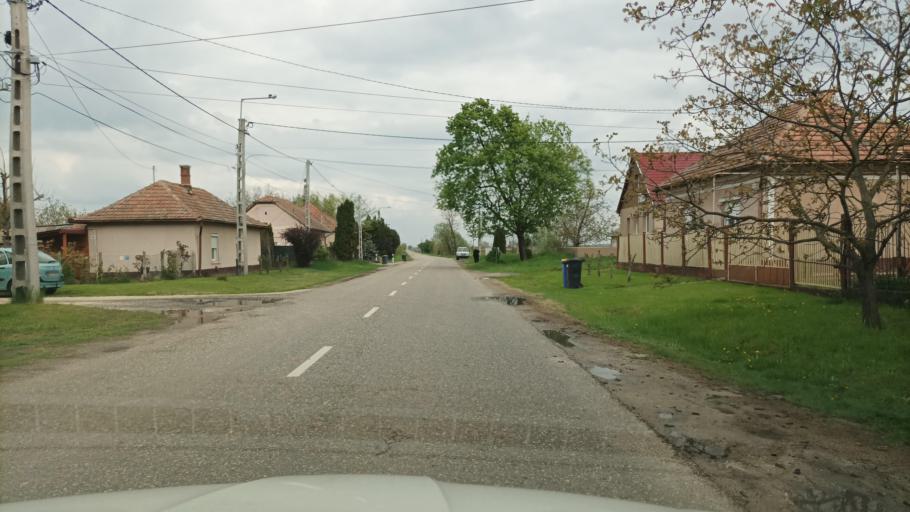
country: HU
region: Pest
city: Tortel
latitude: 47.1222
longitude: 19.9404
